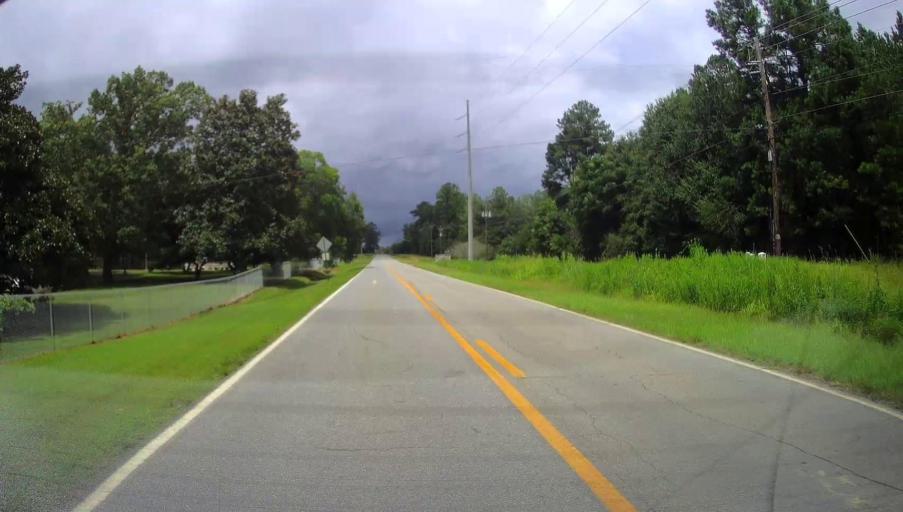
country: US
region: Georgia
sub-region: Bibb County
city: Macon
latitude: 32.8072
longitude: -83.5387
